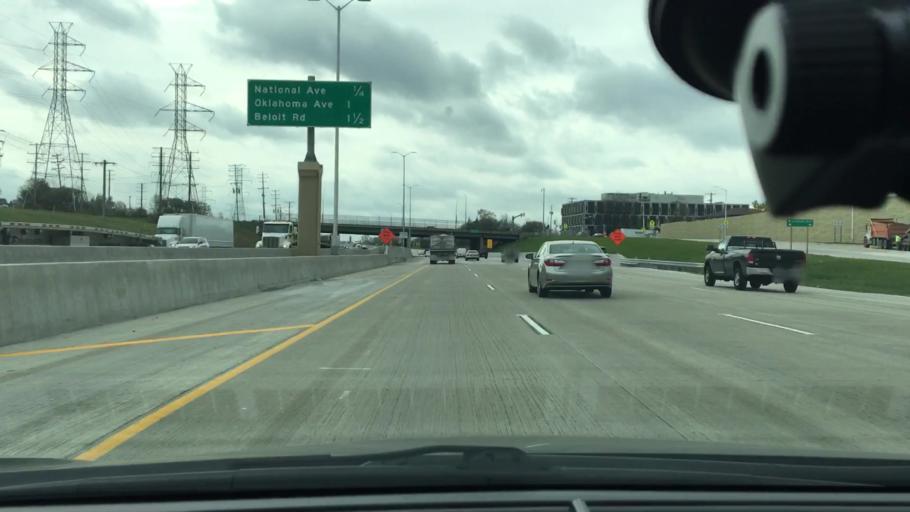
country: US
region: Wisconsin
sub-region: Milwaukee County
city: West Allis
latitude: 43.0047
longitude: -88.0380
